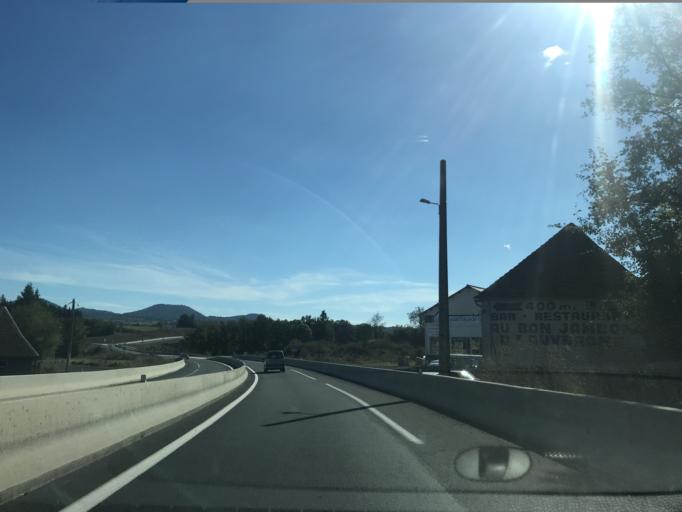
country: FR
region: Auvergne
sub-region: Departement du Puy-de-Dome
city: Gelles
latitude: 45.7368
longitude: 2.8620
